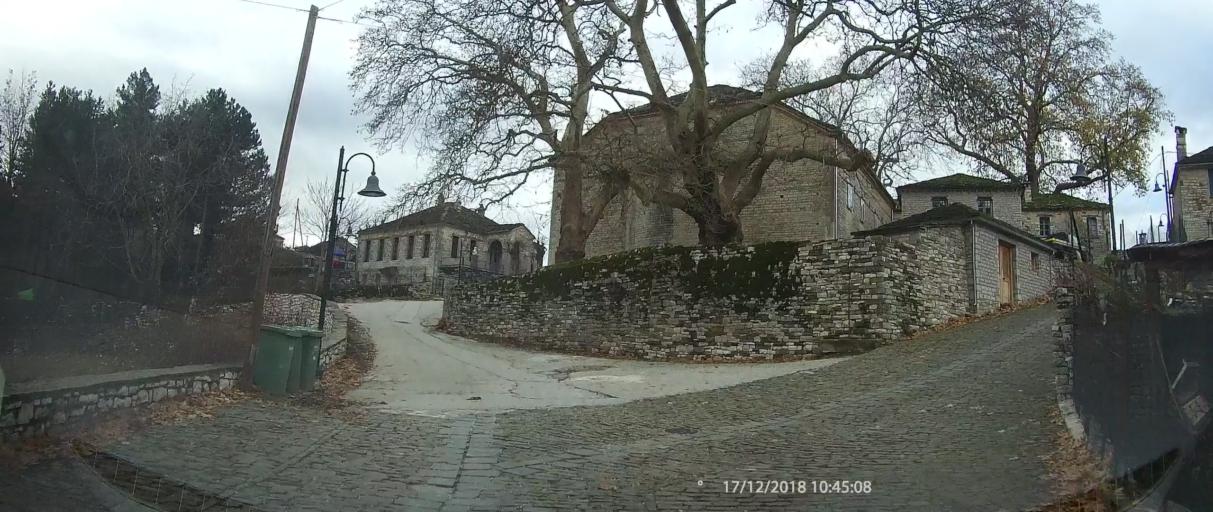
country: GR
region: Epirus
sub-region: Nomos Ioanninon
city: Konitsa
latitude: 39.9682
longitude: 20.7193
